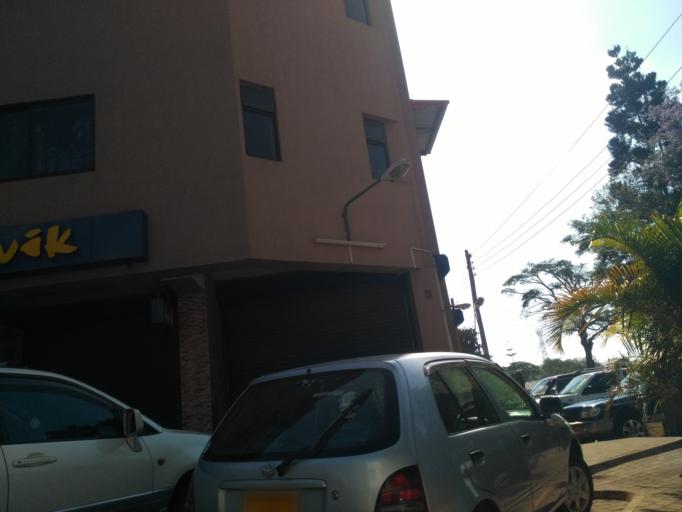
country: TZ
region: Arusha
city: Arusha
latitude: -3.3751
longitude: 36.6888
